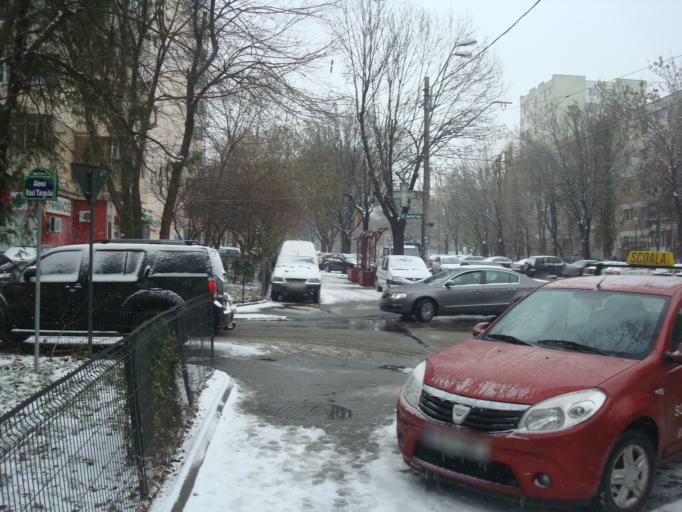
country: RO
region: Ilfov
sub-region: Comuna Popesti-Leordeni
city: Popesti-Leordeni
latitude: 44.3804
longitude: 26.1263
